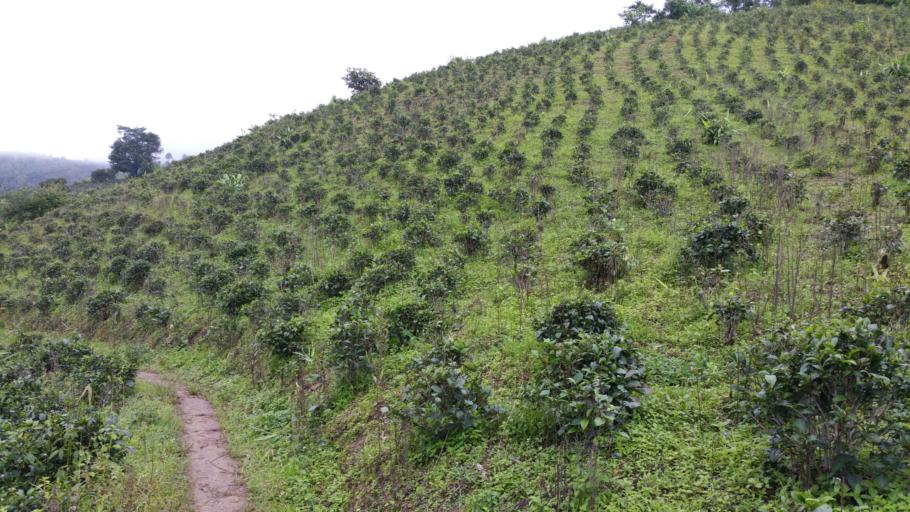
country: MM
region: Mandalay
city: Yamethin
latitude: 20.6122
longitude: 96.5128
